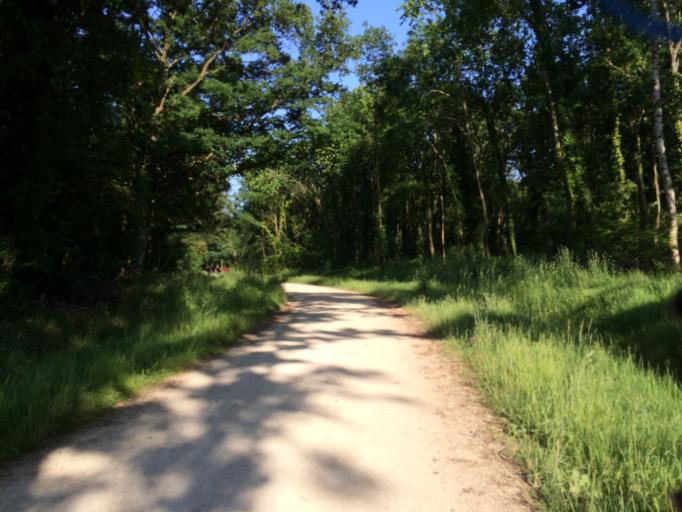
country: FR
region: Ile-de-France
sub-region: Departement de l'Essonne
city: Fleury-Merogis
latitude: 48.6272
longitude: 2.3743
